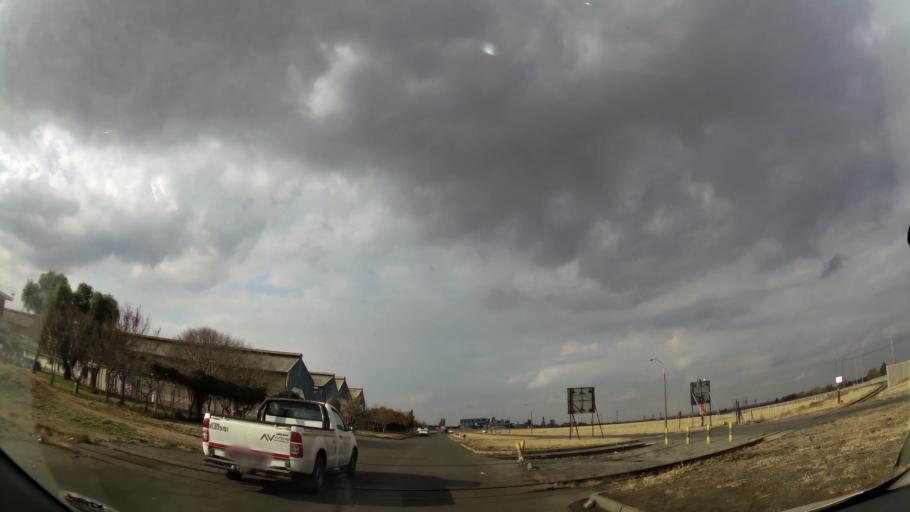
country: ZA
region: Orange Free State
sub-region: Fezile Dabi District Municipality
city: Sasolburg
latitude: -26.8336
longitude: 27.8535
